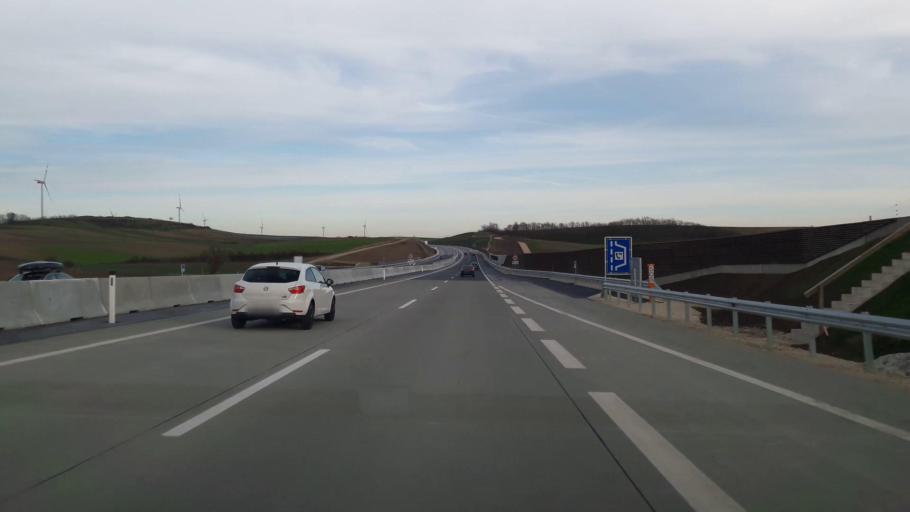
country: AT
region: Lower Austria
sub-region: Politischer Bezirk Mistelbach
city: Wilfersdorf
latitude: 48.6039
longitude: 16.6552
